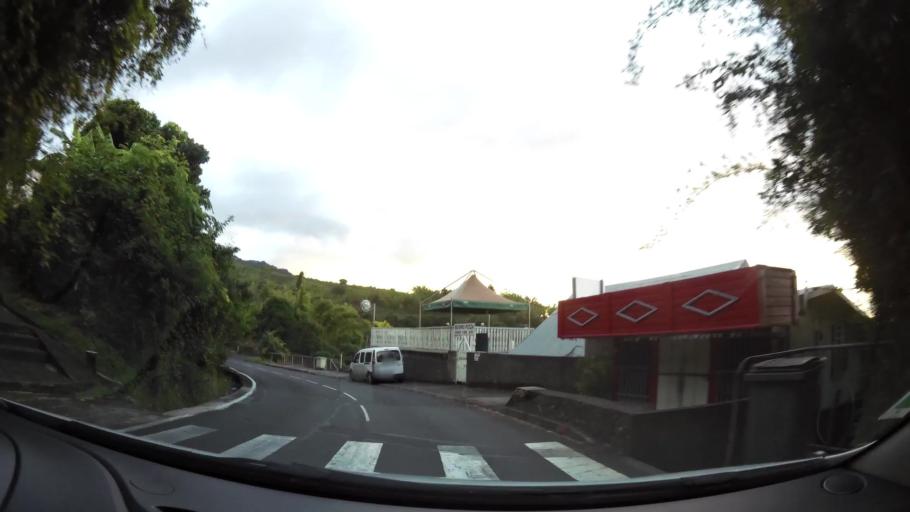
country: RE
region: Reunion
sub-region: Reunion
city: Saint-Denis
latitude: -20.9148
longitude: 55.4606
